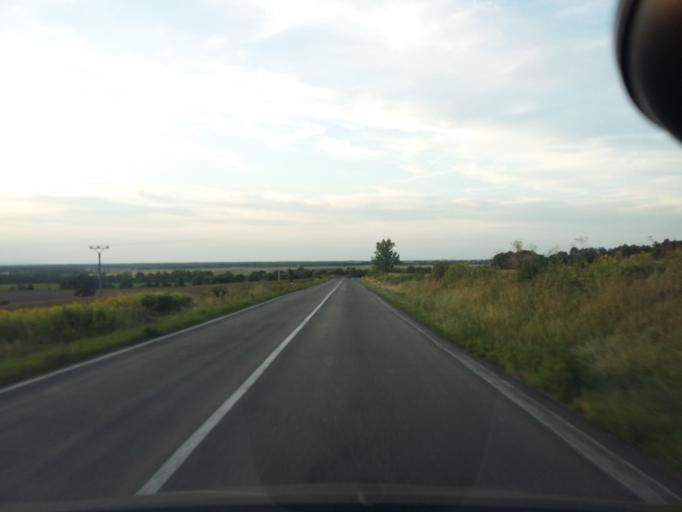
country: SK
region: Bratislavsky
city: Svaty Jur
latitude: 48.3747
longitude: 17.1491
